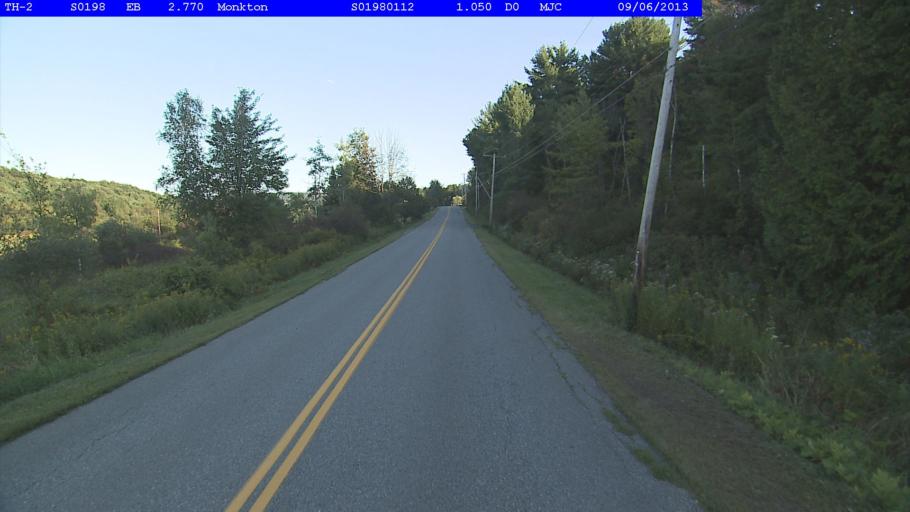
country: US
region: Vermont
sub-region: Chittenden County
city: Hinesburg
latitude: 44.2507
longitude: -73.1766
